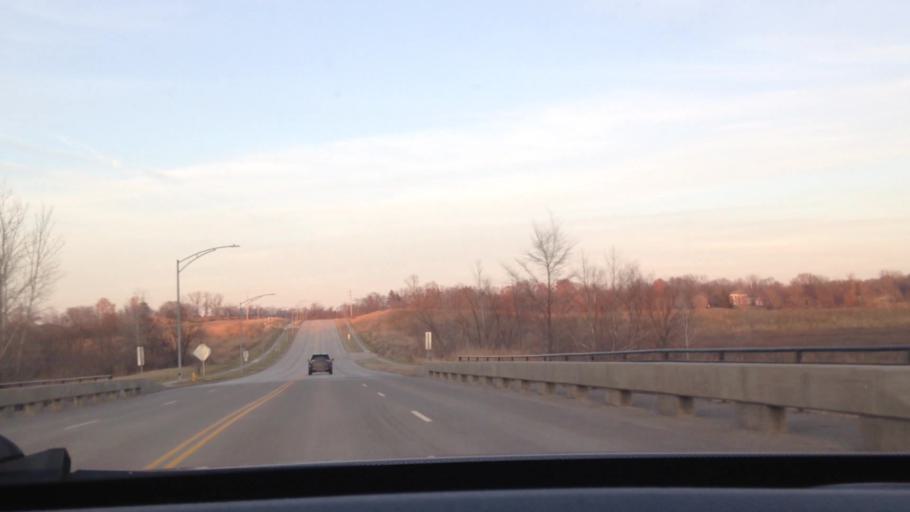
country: US
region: Missouri
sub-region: Clay County
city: Pleasant Valley
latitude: 39.2126
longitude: -94.4436
